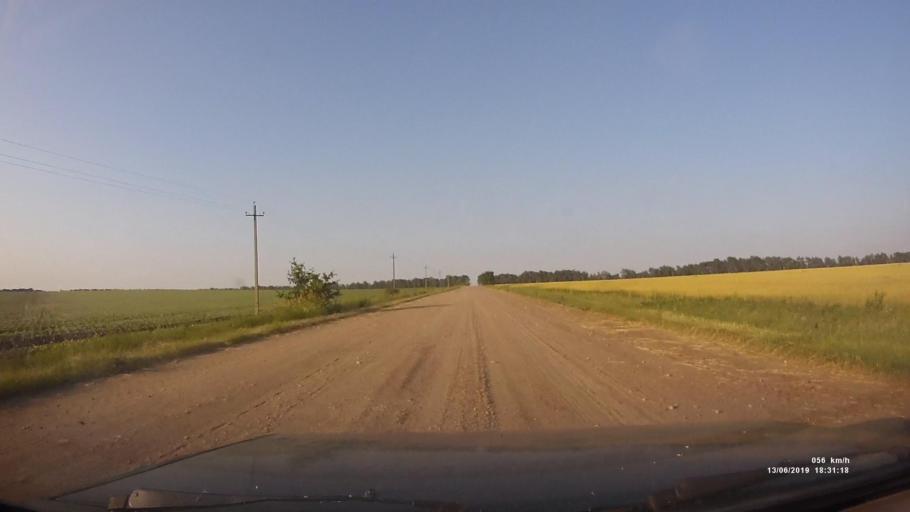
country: RU
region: Rostov
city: Kazanskaya
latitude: 49.8659
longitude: 41.3576
